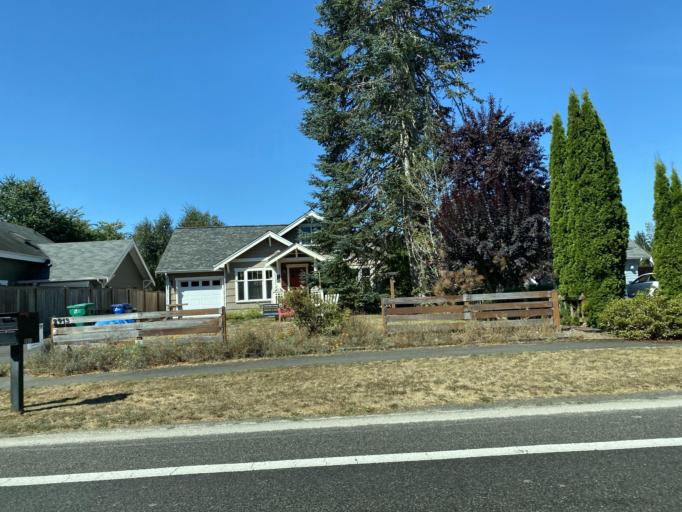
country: US
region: Washington
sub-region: Thurston County
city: Olympia
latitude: 47.0224
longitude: -122.8651
